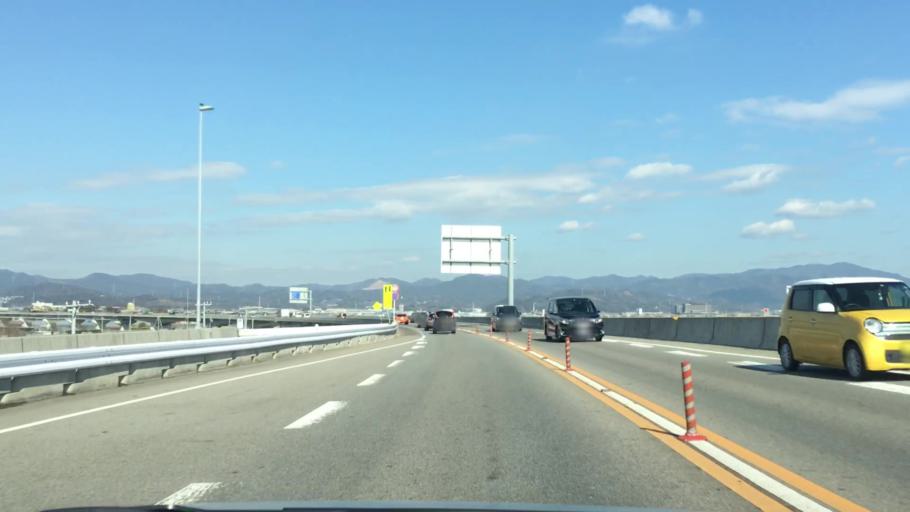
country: JP
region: Aichi
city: Kozakai-cho
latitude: 34.8049
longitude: 137.3375
